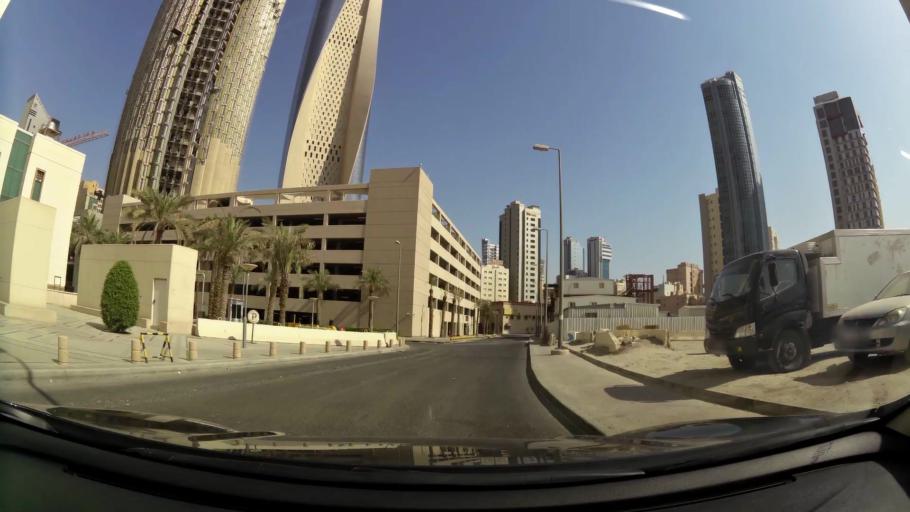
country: KW
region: Al Asimah
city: Ad Dasmah
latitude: 29.3764
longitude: 47.9917
